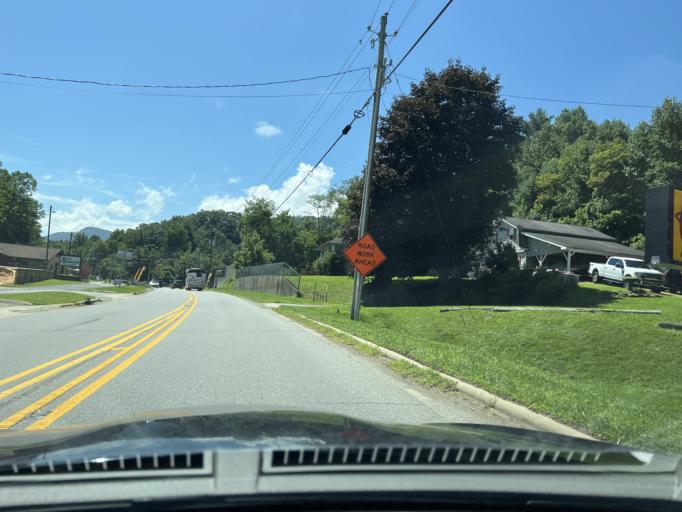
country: US
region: North Carolina
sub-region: Buncombe County
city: Fairview
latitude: 35.5191
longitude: -82.4039
